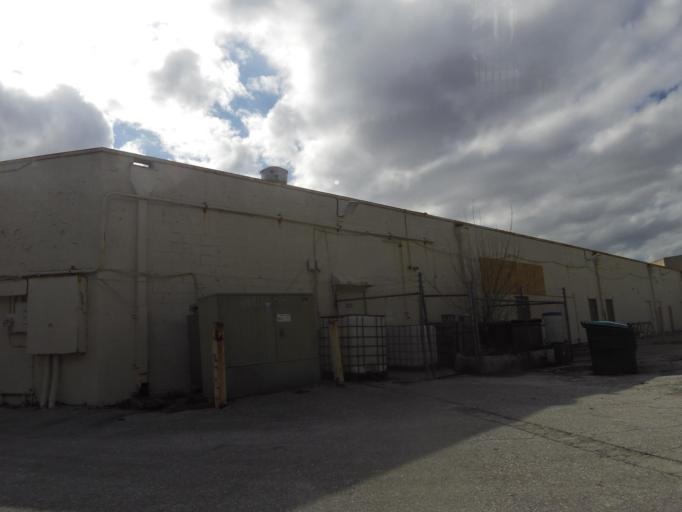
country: US
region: Florida
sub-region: Duval County
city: Jacksonville
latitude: 30.3304
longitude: -81.6017
